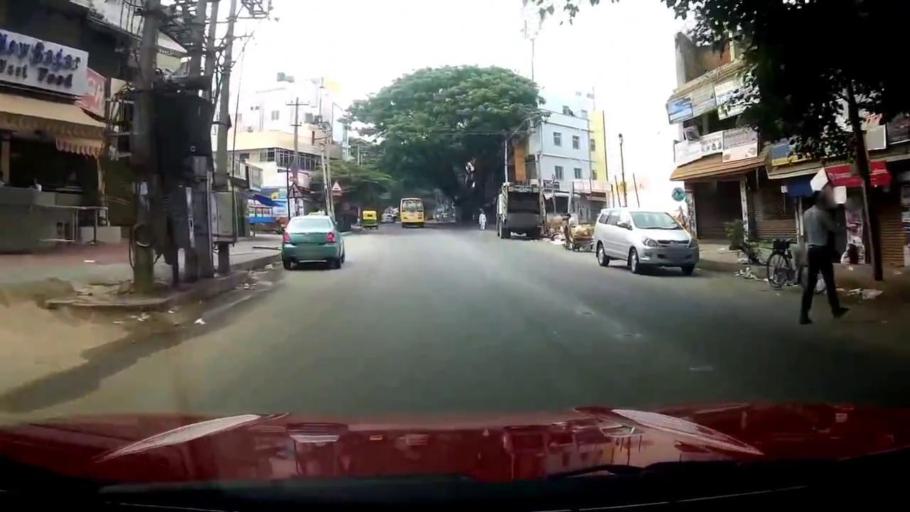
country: IN
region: Karnataka
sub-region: Bangalore Urban
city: Yelahanka
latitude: 13.0382
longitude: 77.5650
